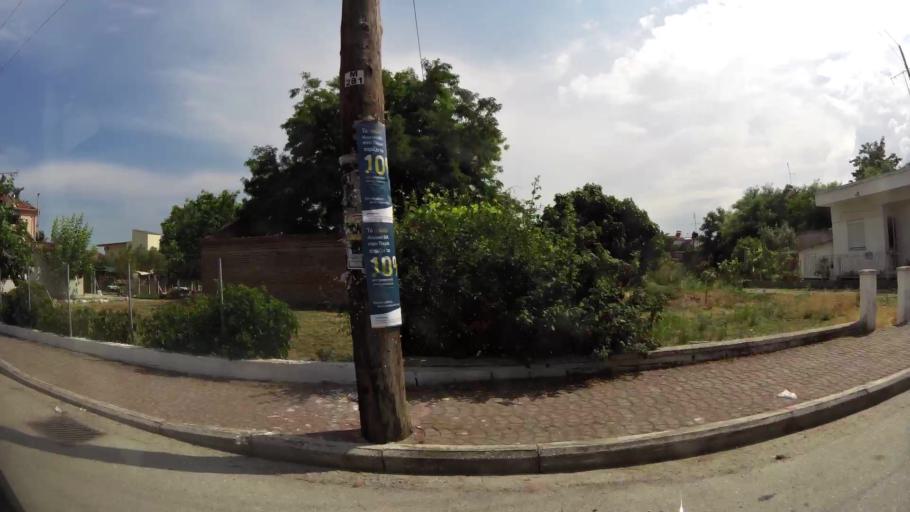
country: GR
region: Central Macedonia
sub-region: Nomos Pierias
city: Korinos
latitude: 40.3147
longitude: 22.5881
